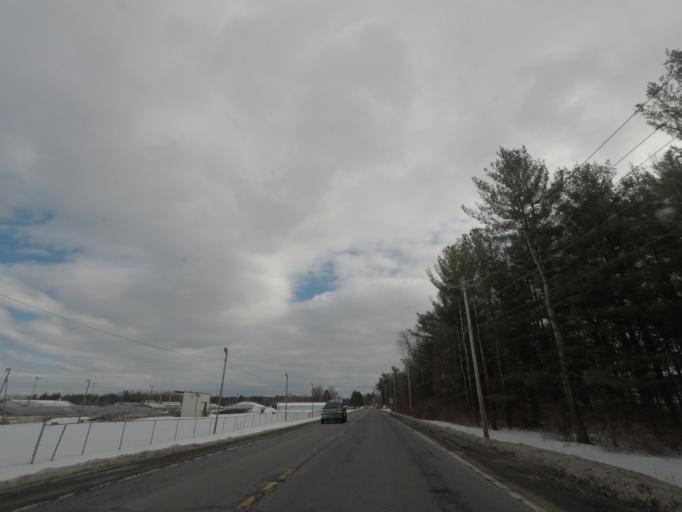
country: US
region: New York
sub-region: Saratoga County
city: Schuylerville
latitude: 43.0929
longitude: -73.5497
